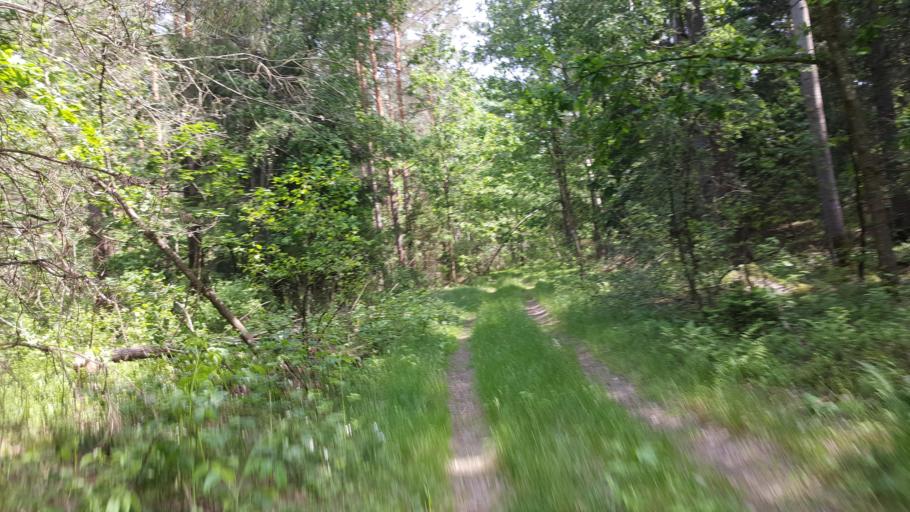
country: BY
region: Brest
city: Kamyanyuki
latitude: 52.5043
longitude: 23.8317
